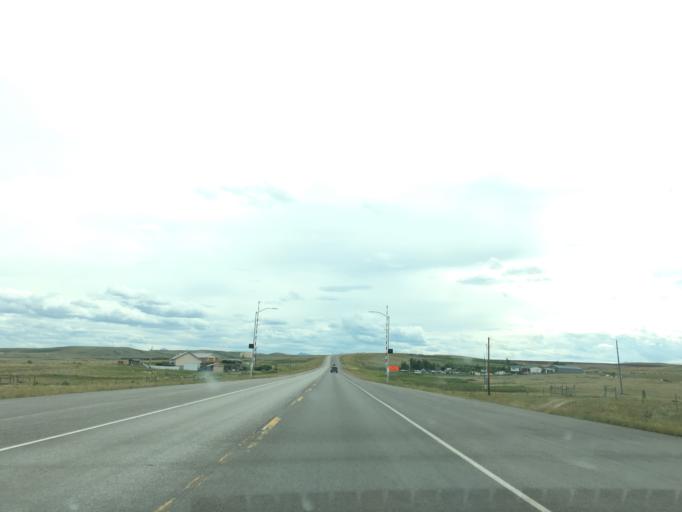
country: US
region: Montana
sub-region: Glacier County
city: South Browning
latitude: 48.5511
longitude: -113.0258
